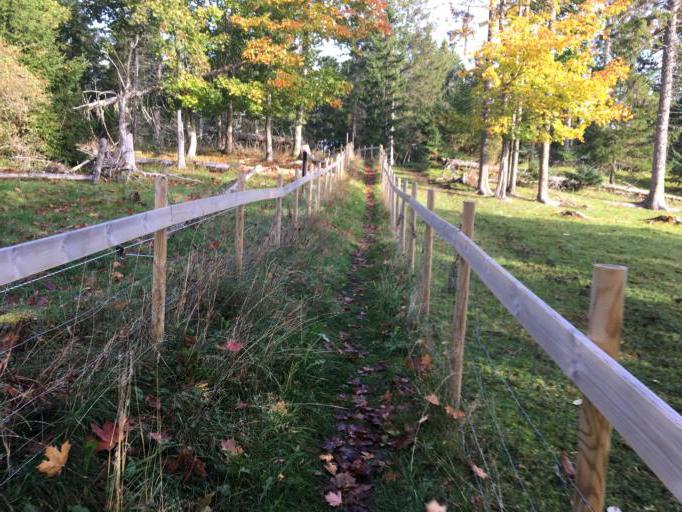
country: NO
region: Nord-Trondelag
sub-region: Leksvik
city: Leksvik
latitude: 63.5725
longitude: 10.6127
